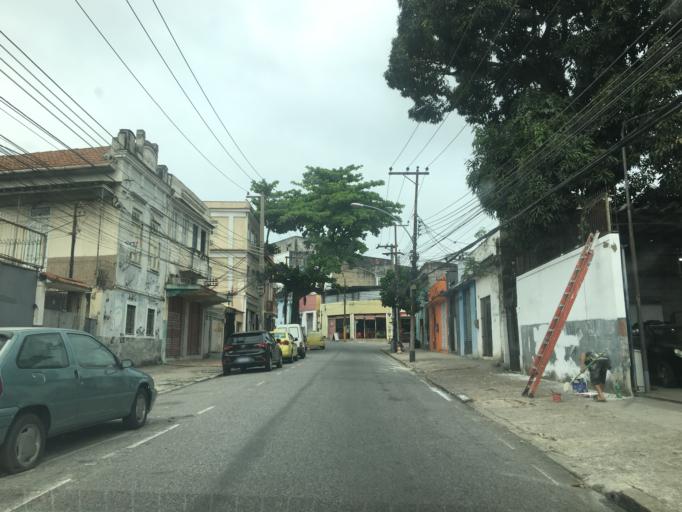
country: BR
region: Rio de Janeiro
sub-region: Rio De Janeiro
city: Rio de Janeiro
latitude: -22.8950
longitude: -43.2286
